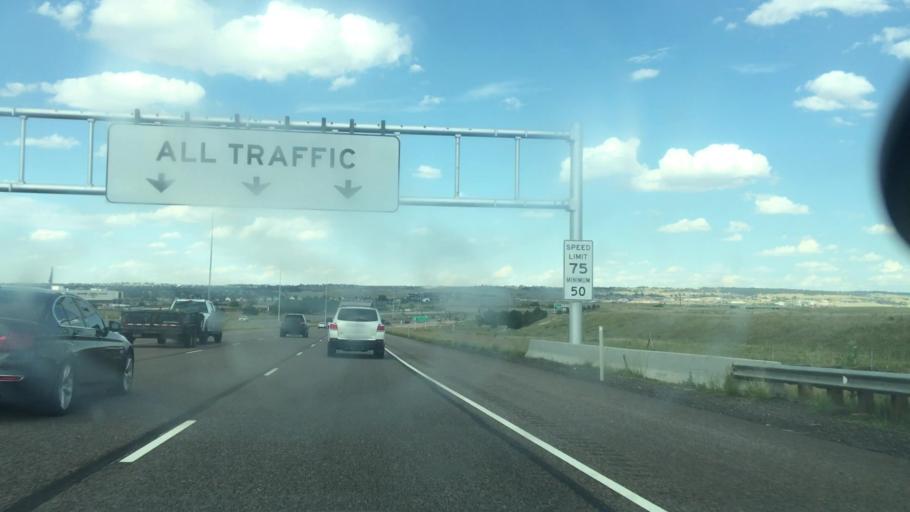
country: US
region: Colorado
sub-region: Arapahoe County
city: Dove Valley
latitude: 39.5548
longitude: -104.8291
